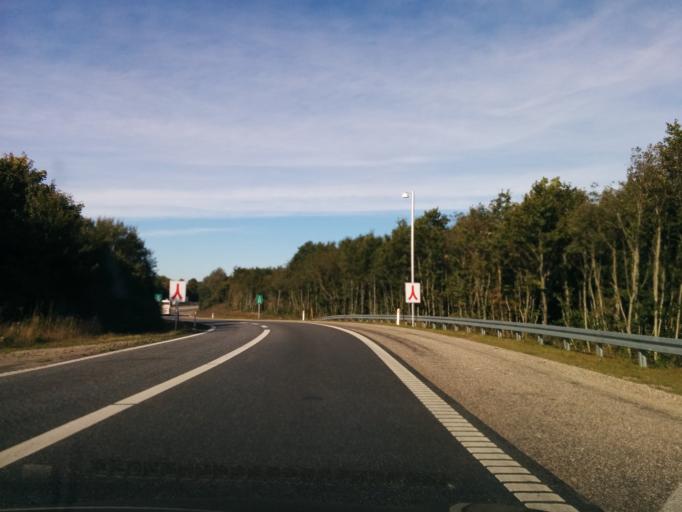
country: DK
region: South Denmark
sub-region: Kolding Kommune
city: Kolding
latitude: 55.4664
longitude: 9.4399
